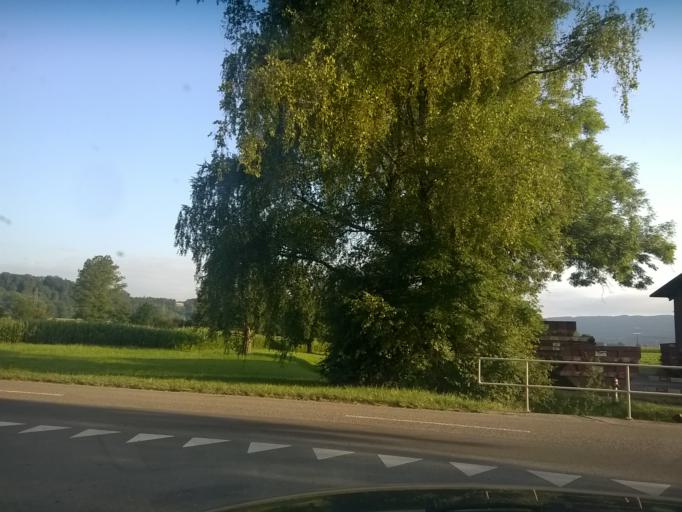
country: CH
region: Zurich
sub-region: Bezirk Buelach
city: Embrach / Embrach (Dorfkern)
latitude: 47.4921
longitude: 8.6019
